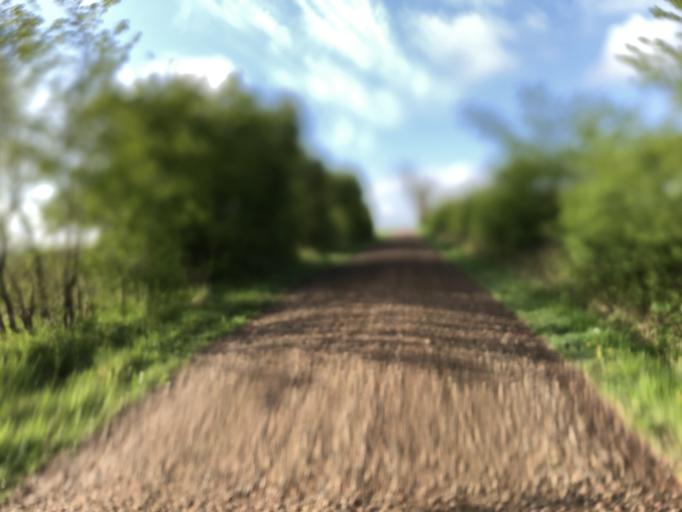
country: SE
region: Skane
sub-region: Lunds Kommun
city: Lund
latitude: 55.6941
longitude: 13.2713
